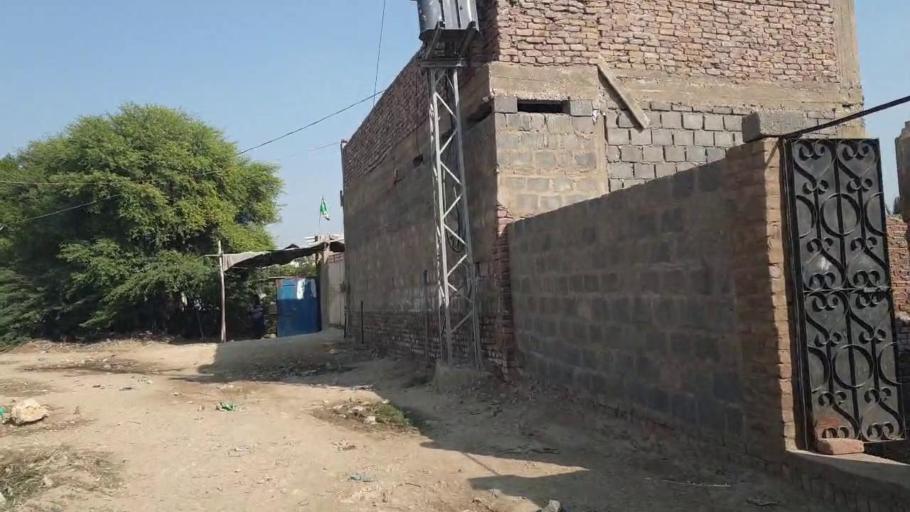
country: PK
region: Sindh
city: Kotri
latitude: 25.3620
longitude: 68.2856
